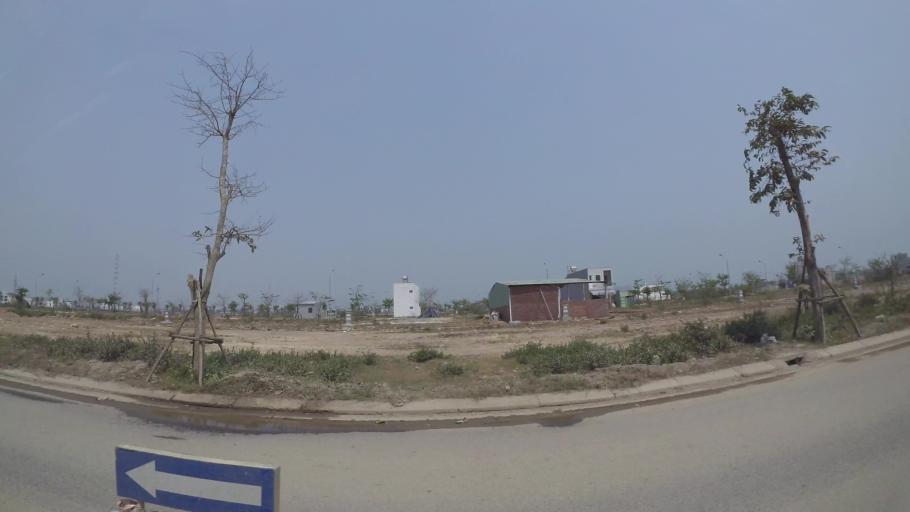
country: VN
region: Da Nang
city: Ngu Hanh Son
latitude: 16.0133
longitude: 108.2377
